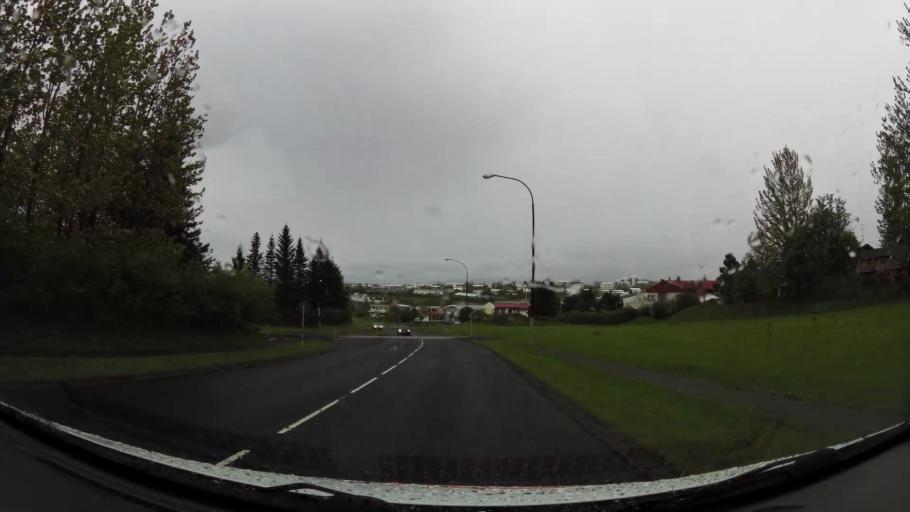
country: IS
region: Capital Region
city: Gardabaer
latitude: 64.0903
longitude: -21.9037
